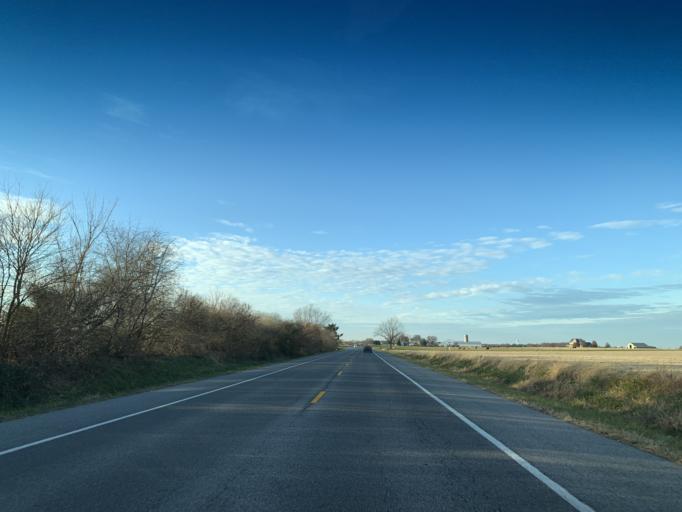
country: US
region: Maryland
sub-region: Kent County
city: Chestertown
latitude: 39.2552
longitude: -76.0804
